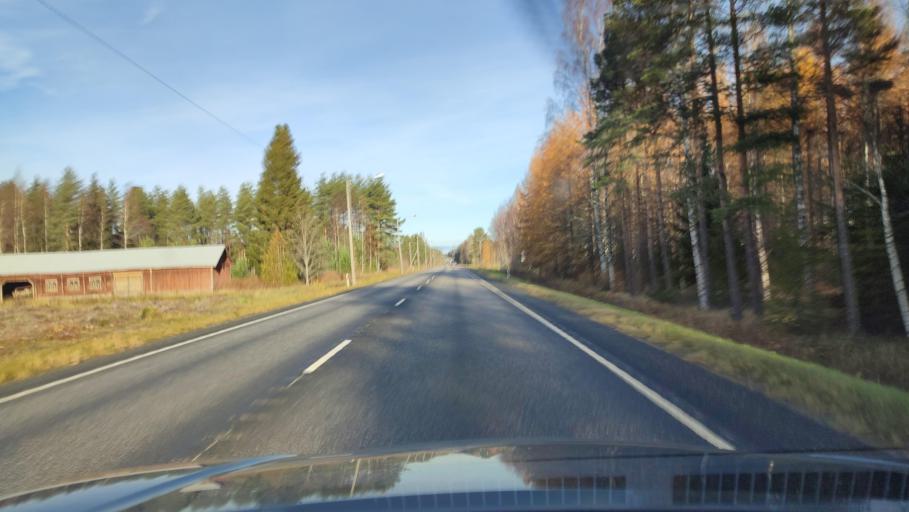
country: FI
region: Ostrobothnia
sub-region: Vaasa
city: Malax
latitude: 62.8036
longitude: 21.6782
